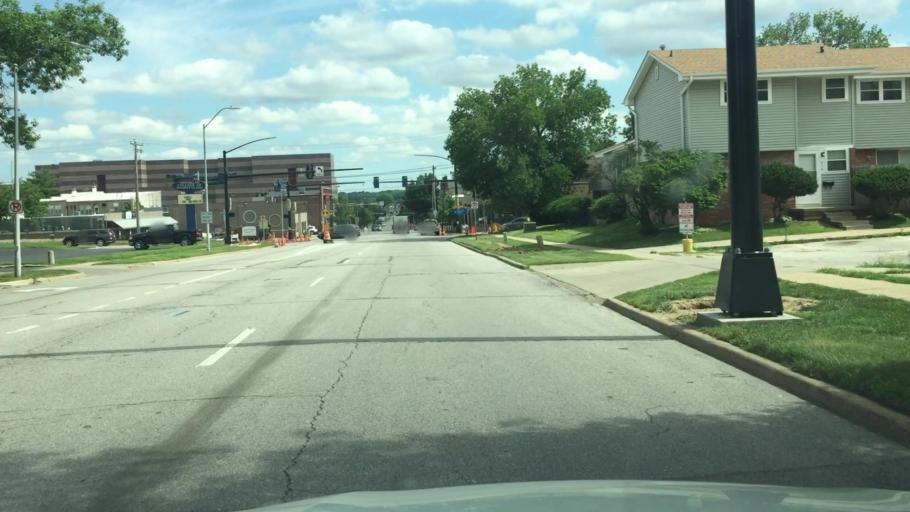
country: US
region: Iowa
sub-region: Polk County
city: Des Moines
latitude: 41.5928
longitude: -93.6110
